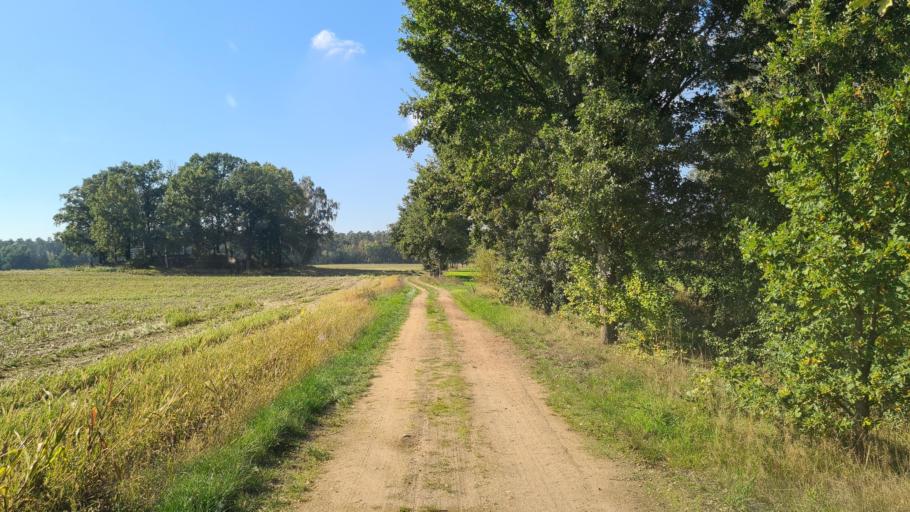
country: DE
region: Brandenburg
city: Lebusa
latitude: 51.8256
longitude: 13.4428
